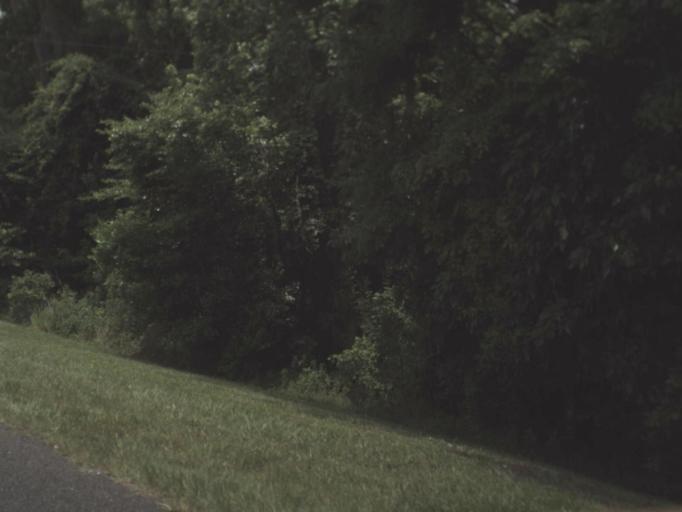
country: US
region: Florida
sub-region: Putnam County
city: East Palatka
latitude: 29.6222
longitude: -81.5863
